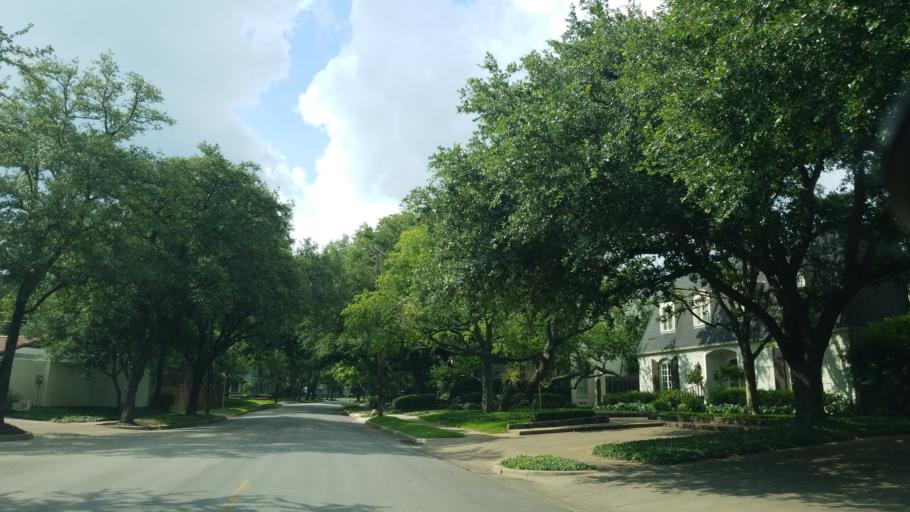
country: US
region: Texas
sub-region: Dallas County
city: University Park
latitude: 32.8423
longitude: -96.8069
